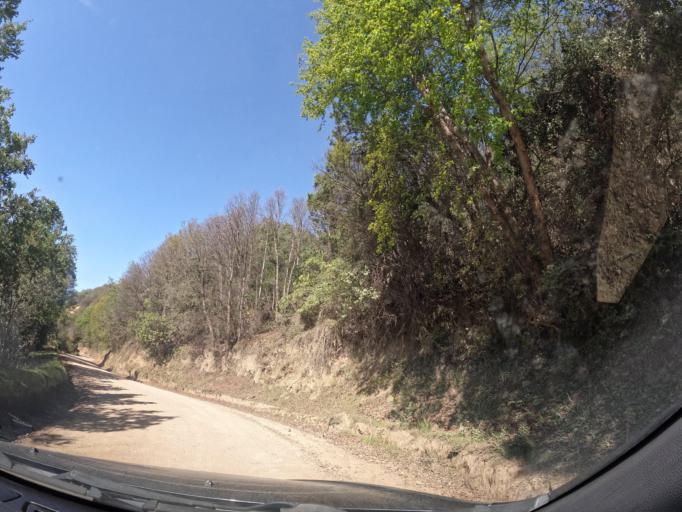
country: CL
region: Maule
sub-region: Provincia de Linares
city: Longavi
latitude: -36.2430
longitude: -71.4396
